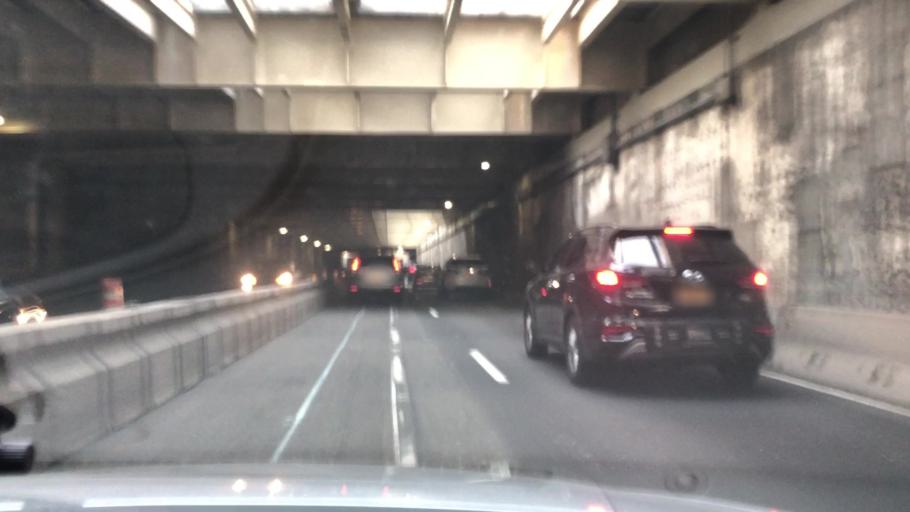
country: US
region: New Jersey
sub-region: Hudson County
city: Hoboken
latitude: 40.7324
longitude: -74.0532
